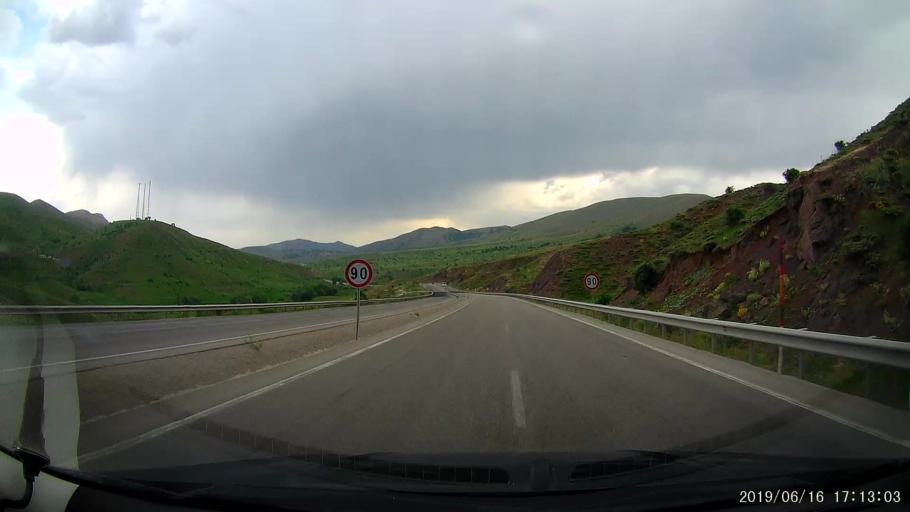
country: TR
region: Erzurum
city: Askale
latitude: 39.8596
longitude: 40.6077
